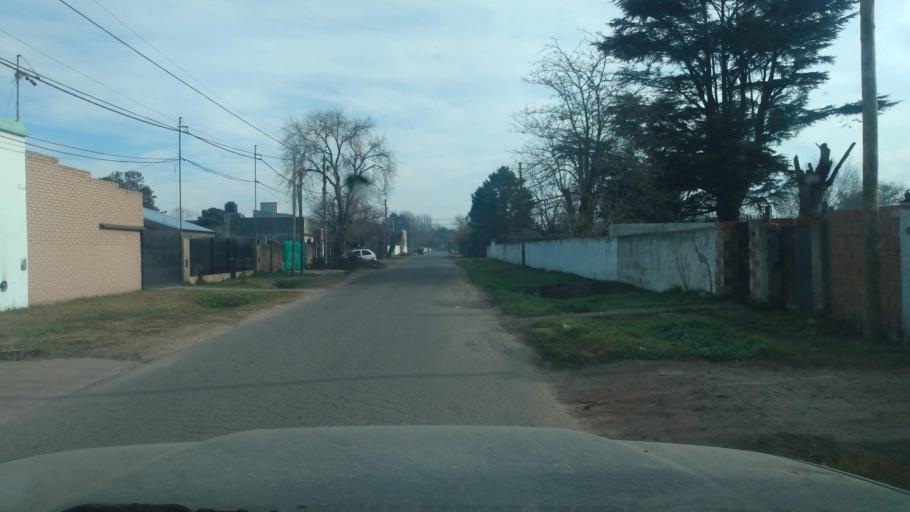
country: AR
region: Buenos Aires
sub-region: Partido de Lujan
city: Lujan
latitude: -34.5437
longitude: -59.1196
